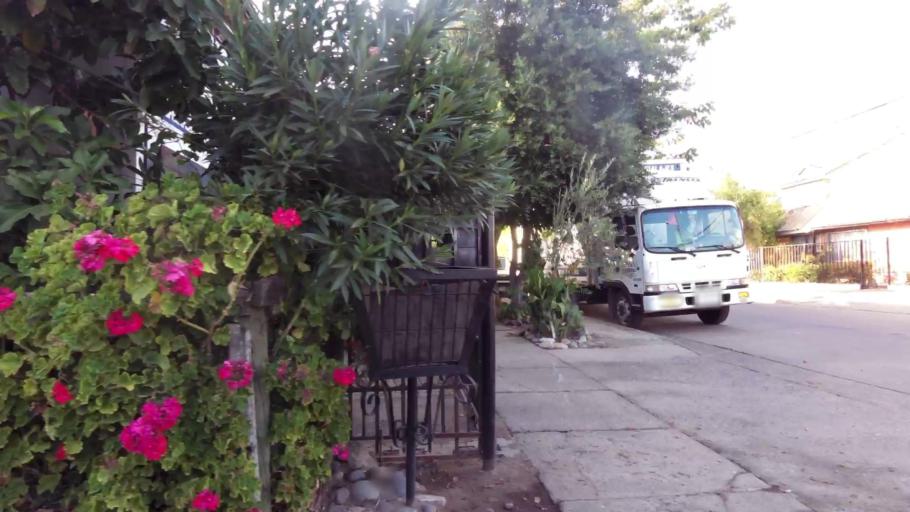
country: CL
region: Maule
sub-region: Provincia de Talca
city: Talca
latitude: -35.4112
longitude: -71.6530
